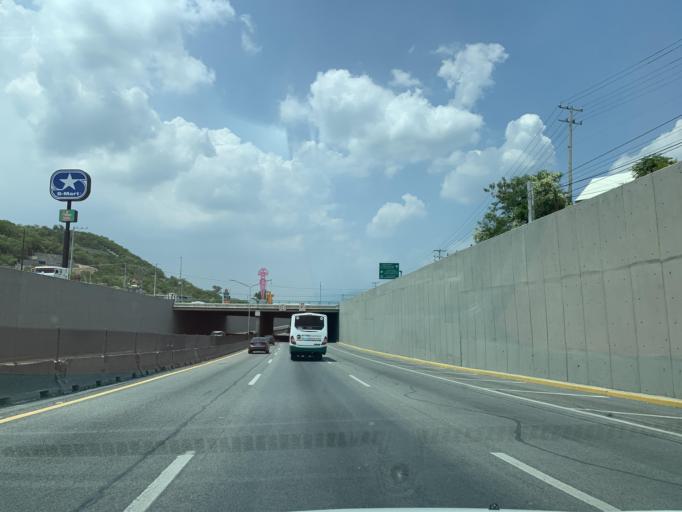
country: MX
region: Nuevo Leon
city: Santiago
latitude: 25.4306
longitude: -100.1512
